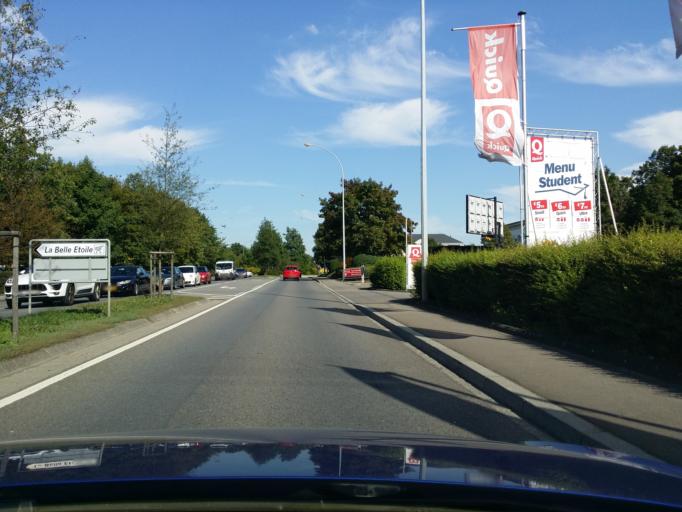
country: LU
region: Luxembourg
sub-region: Canton de Luxembourg
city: Bertrange
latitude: 49.6218
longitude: 6.0497
